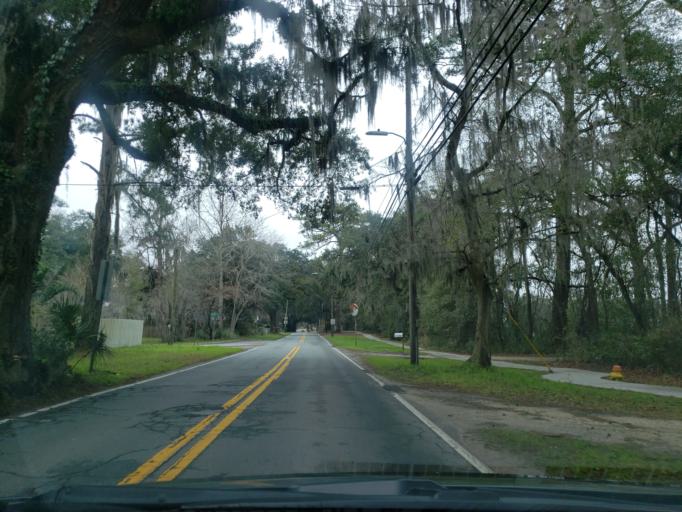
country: US
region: Georgia
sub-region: Chatham County
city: Montgomery
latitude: 31.9505
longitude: -81.1460
